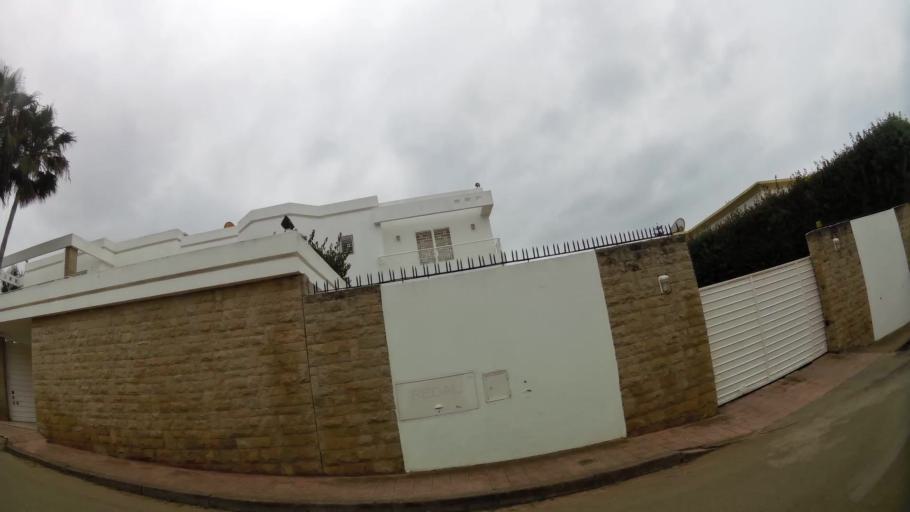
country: MA
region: Rabat-Sale-Zemmour-Zaer
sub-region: Rabat
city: Rabat
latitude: 33.9579
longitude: -6.8144
